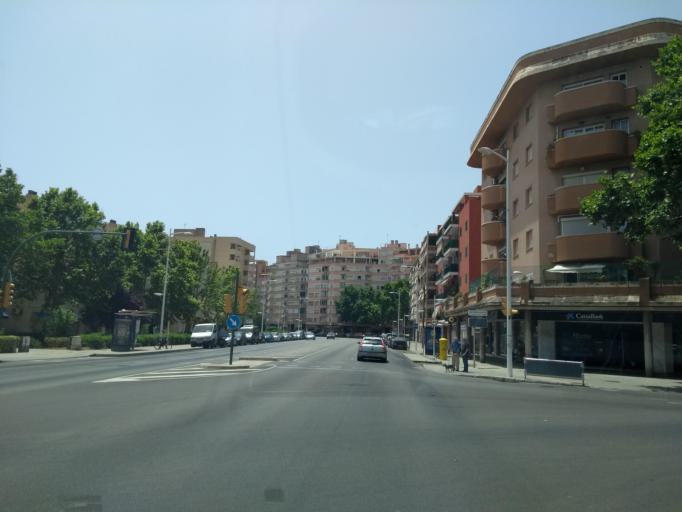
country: ES
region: Balearic Islands
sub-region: Illes Balears
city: Palma
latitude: 39.5871
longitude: 2.6637
